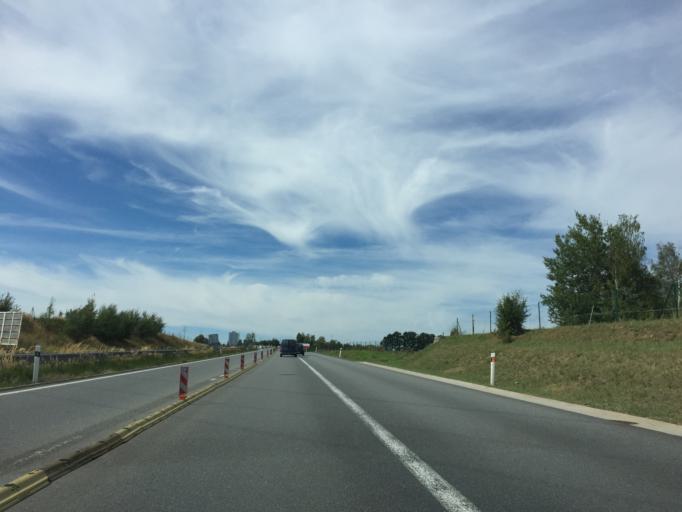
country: CZ
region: Jihocesky
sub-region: Okres Tabor
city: Sezimovo Usti
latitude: 49.4105
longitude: 14.7140
